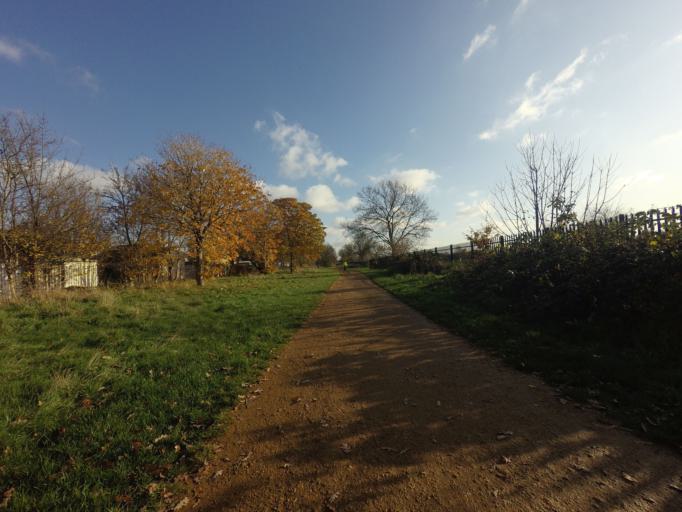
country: GB
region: England
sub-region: Greater London
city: Feltham
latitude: 51.4444
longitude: -0.3992
